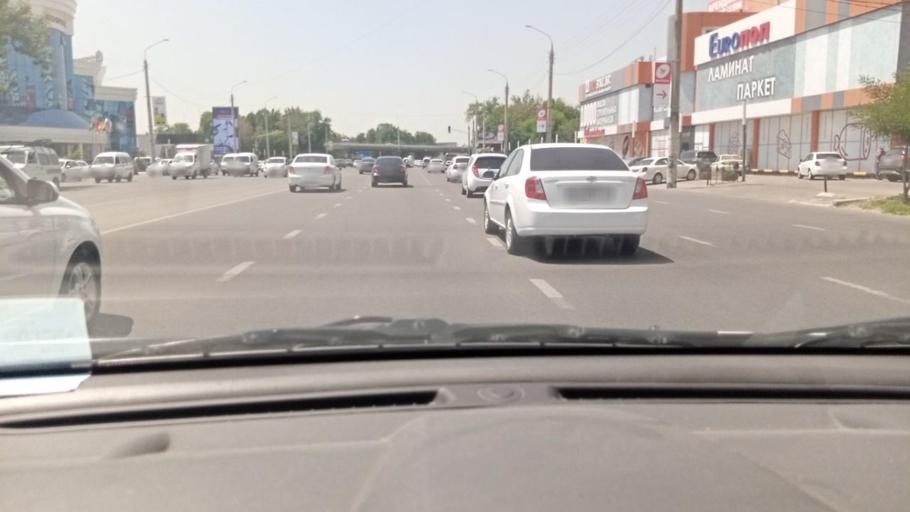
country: UZ
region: Toshkent Shahri
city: Tashkent
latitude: 41.2702
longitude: 69.2642
